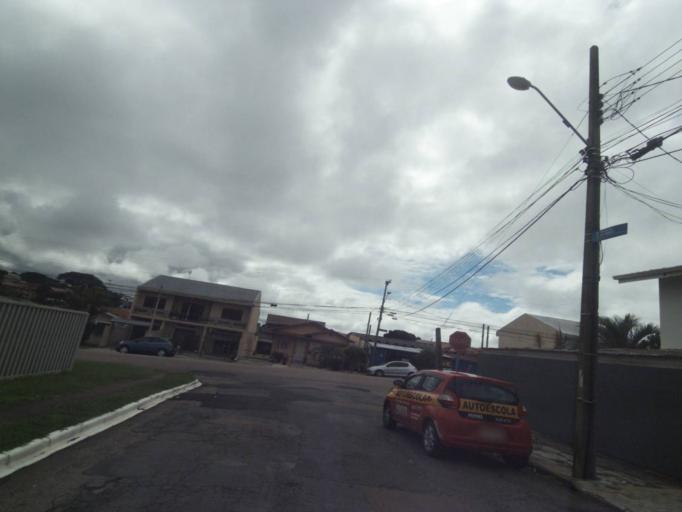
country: BR
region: Parana
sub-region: Curitiba
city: Curitiba
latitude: -25.4798
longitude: -49.2819
